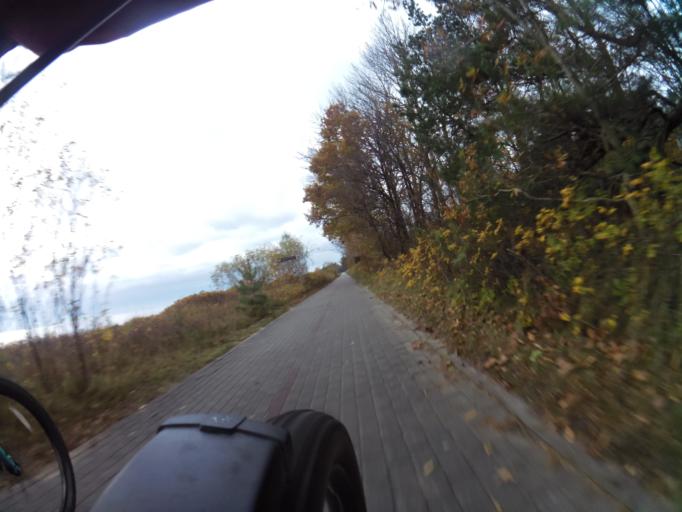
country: PL
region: Pomeranian Voivodeship
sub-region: Powiat pucki
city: Puck
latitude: 54.7460
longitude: 18.5464
